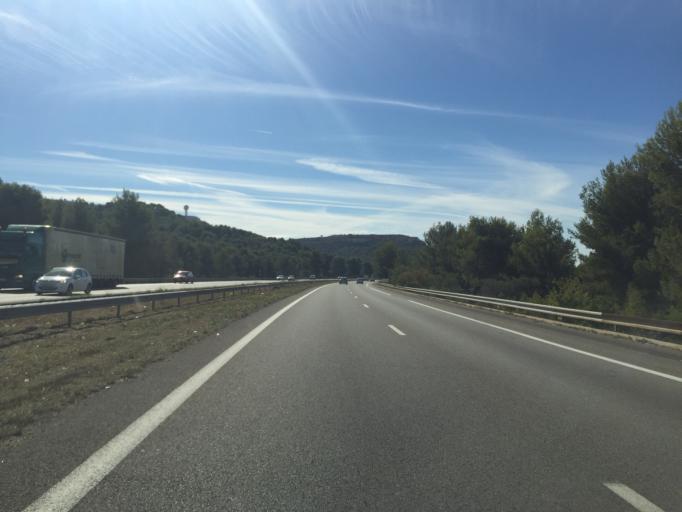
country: FR
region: Provence-Alpes-Cote d'Azur
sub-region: Departement des Bouches-du-Rhone
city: Rognac
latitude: 43.4843
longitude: 5.2408
